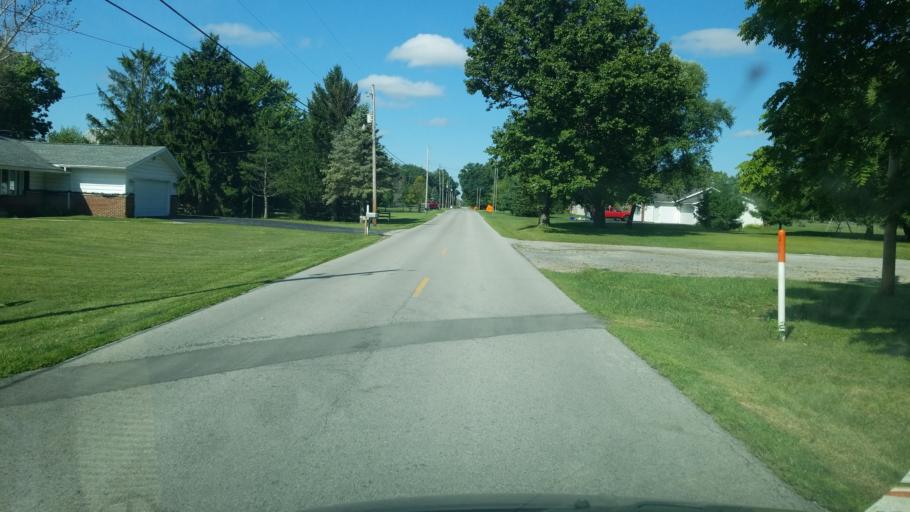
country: US
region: Ohio
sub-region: Hancock County
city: Findlay
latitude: 41.1094
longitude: -83.6351
